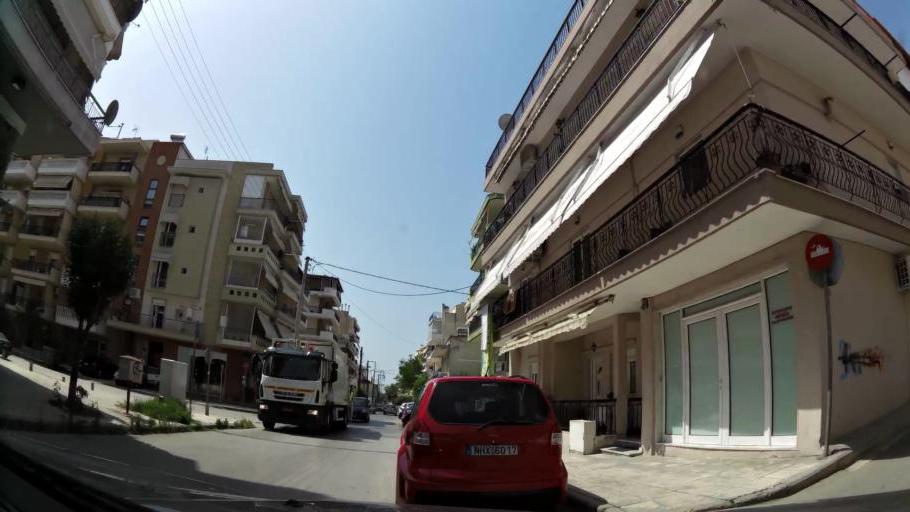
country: GR
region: Central Macedonia
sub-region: Nomos Thessalonikis
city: Evosmos
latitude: 40.6721
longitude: 22.9156
